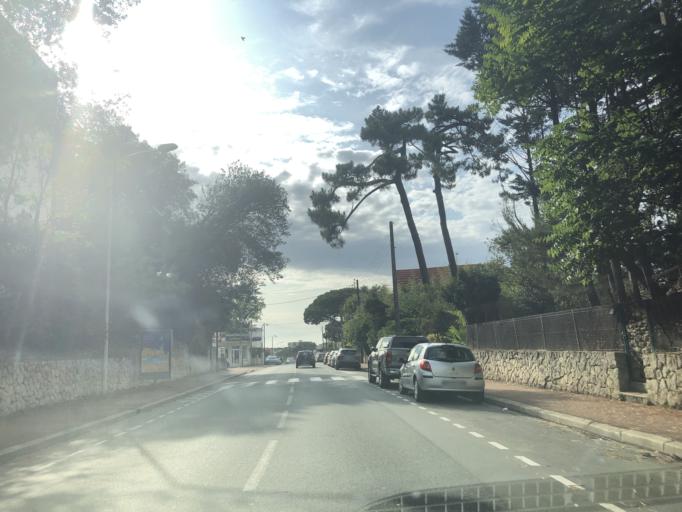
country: FR
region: Poitou-Charentes
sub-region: Departement de la Charente-Maritime
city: Royan
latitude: 45.6248
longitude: -1.0468
